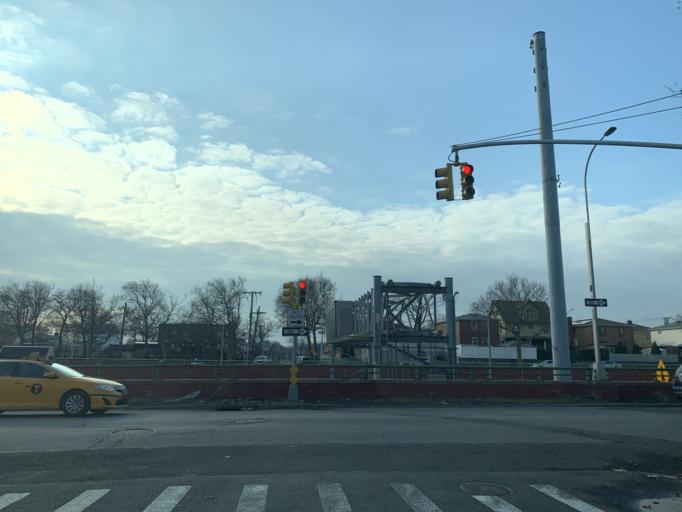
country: US
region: New York
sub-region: Queens County
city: Jamaica
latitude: 40.7431
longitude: -73.8276
